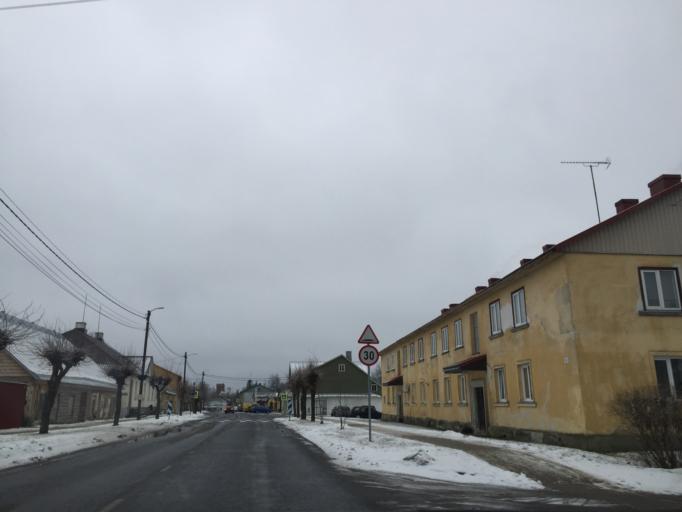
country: EE
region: Laeaene
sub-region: Lihula vald
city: Lihula
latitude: 58.6898
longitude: 23.8359
